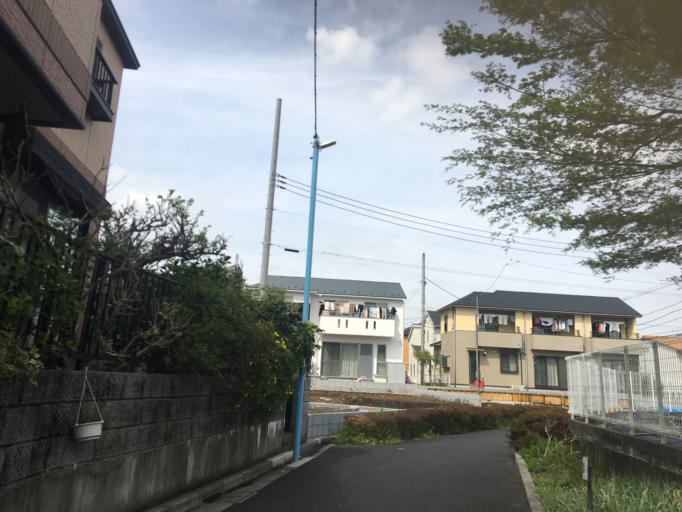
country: JP
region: Tokyo
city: Musashino
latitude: 35.7219
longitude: 139.6155
